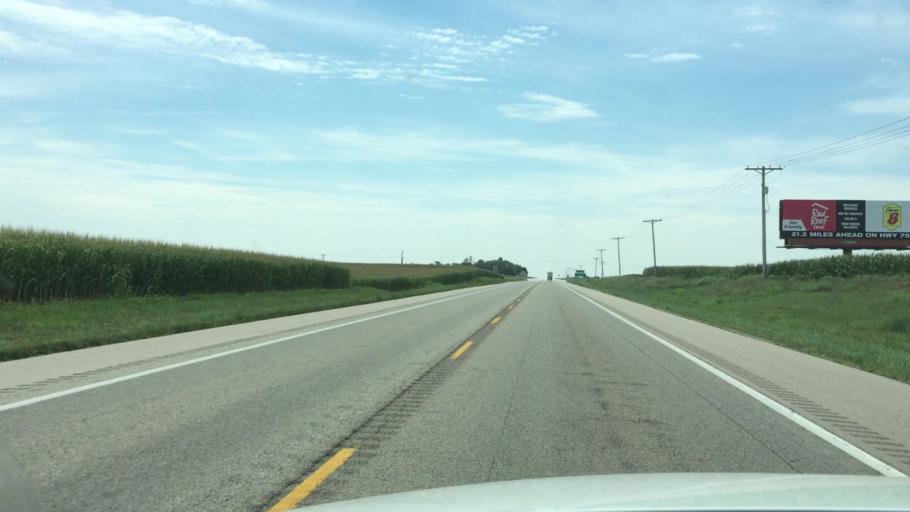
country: US
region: Kansas
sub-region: Nemaha County
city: Sabetha
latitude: 39.7581
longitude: -95.7297
